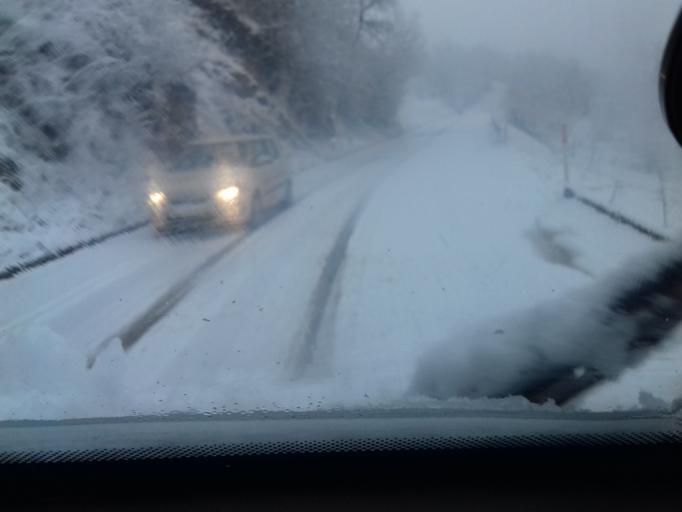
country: BA
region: Federation of Bosnia and Herzegovina
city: Lokvine
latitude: 44.2386
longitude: 17.8187
